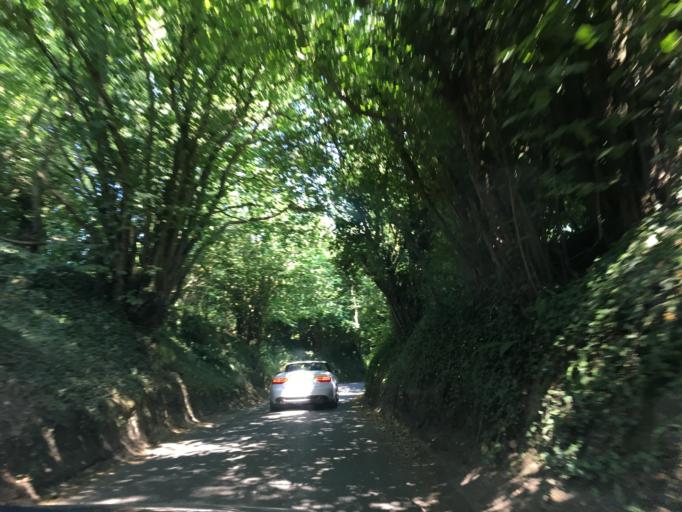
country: GB
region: England
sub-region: Isle of Wight
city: Newchurch
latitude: 50.6773
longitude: -1.2140
